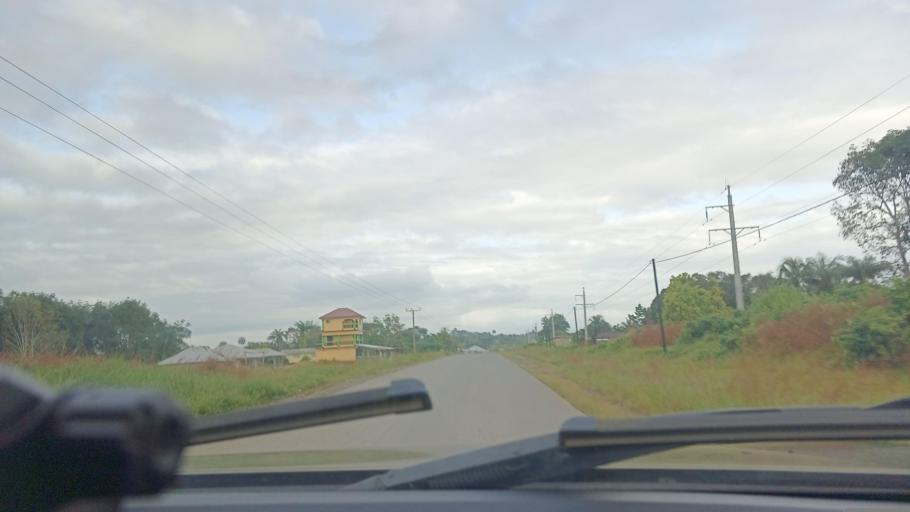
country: LR
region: Montserrado
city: Monrovia
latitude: 6.5705
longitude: -10.8784
